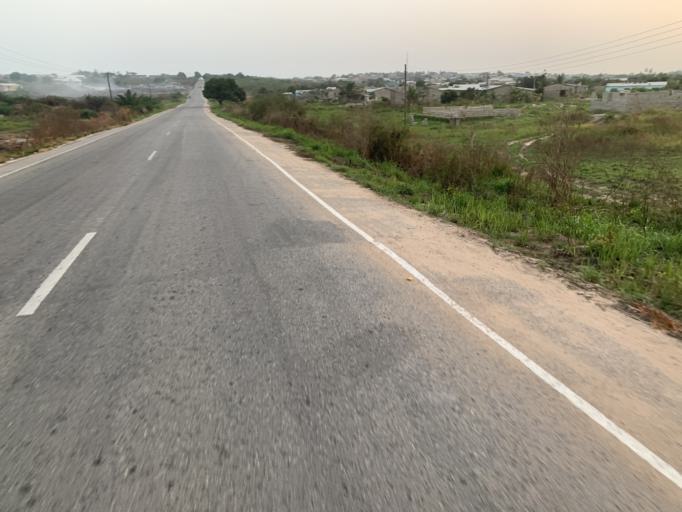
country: GH
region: Central
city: Winneba
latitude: 5.3663
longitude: -0.6083
